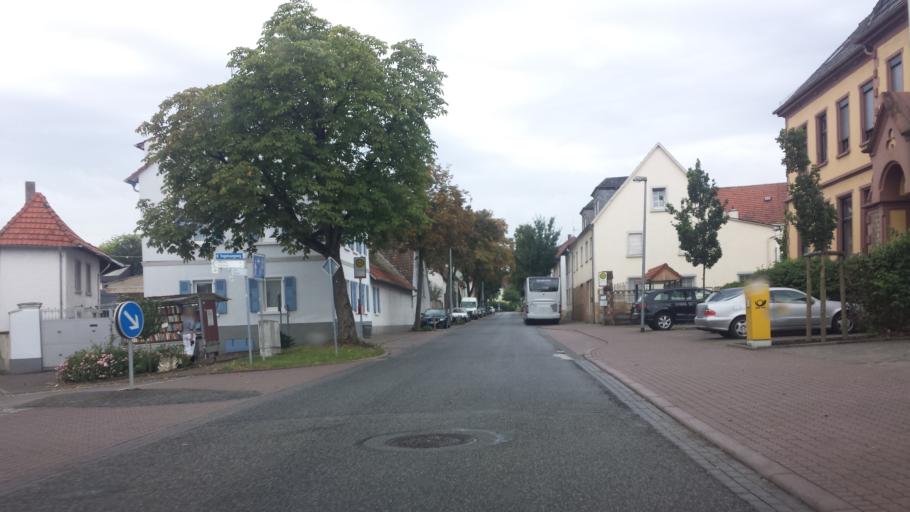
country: DE
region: Rheinland-Pfalz
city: Westhofen
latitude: 49.7023
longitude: 8.2483
